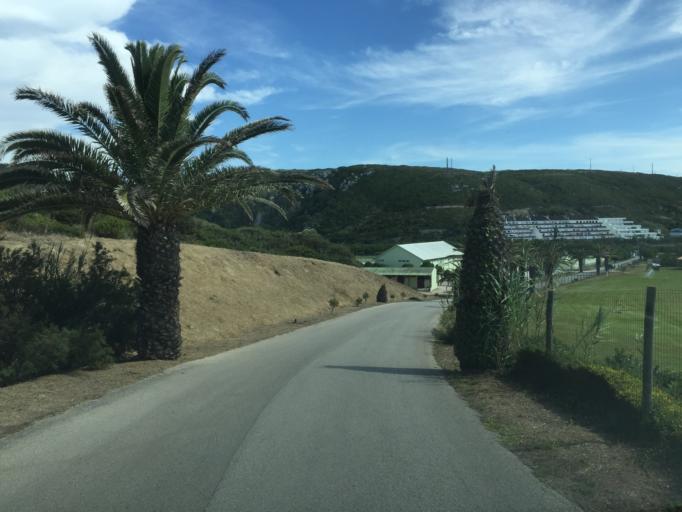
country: PT
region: Lisbon
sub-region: Torres Vedras
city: A dos Cunhados
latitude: 39.1808
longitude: -9.3520
